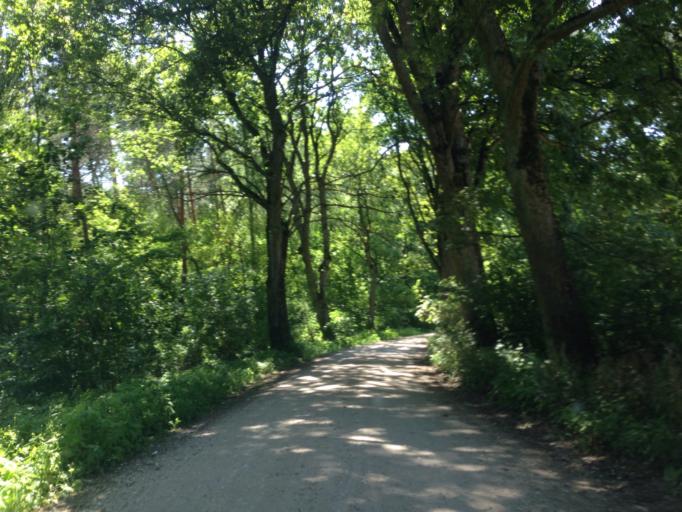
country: PL
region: Kujawsko-Pomorskie
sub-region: Powiat brodnicki
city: Gorzno
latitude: 53.2428
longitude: 19.6638
